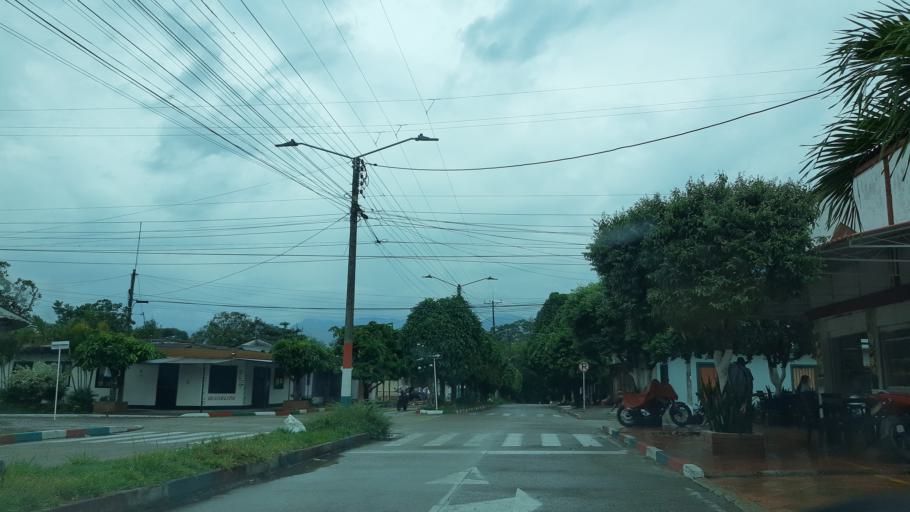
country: CO
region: Casanare
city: Monterrey
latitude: 4.8760
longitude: -72.8942
